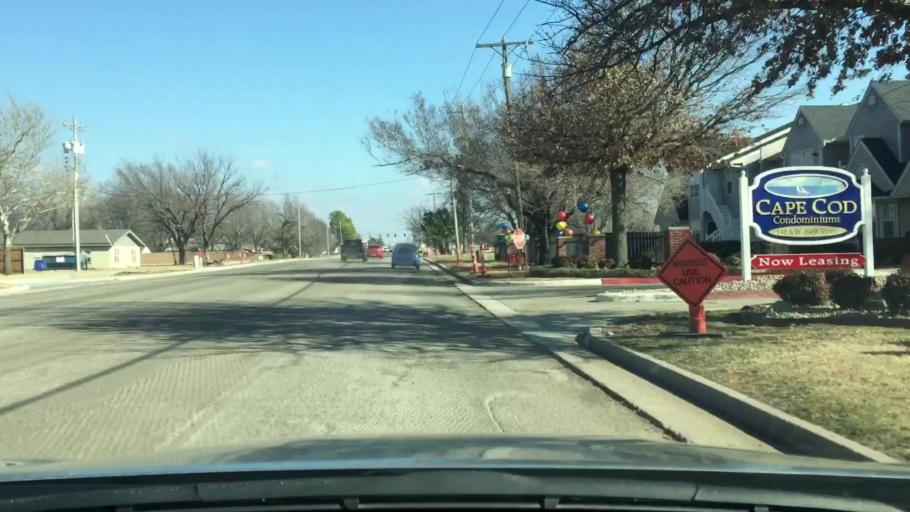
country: US
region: Oklahoma
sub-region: Cleveland County
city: Moore
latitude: 35.3772
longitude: -97.5164
